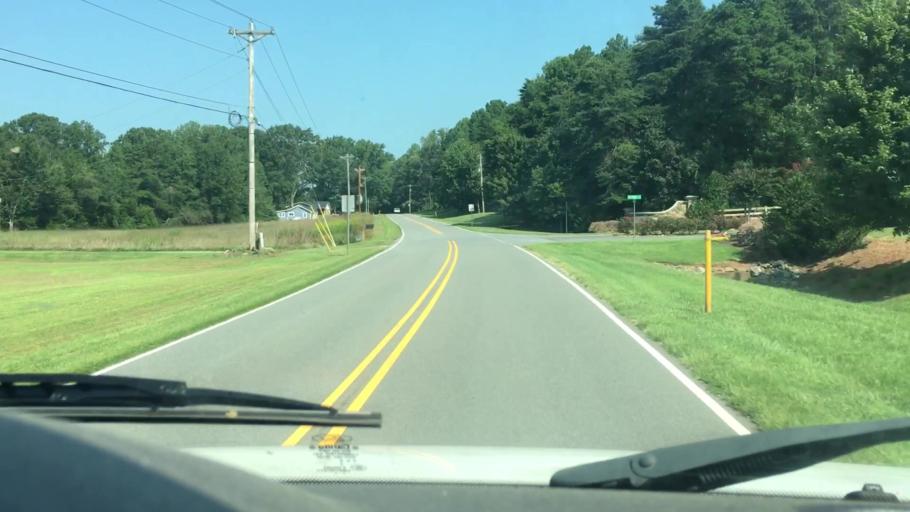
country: US
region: North Carolina
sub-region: Gaston County
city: Davidson
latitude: 35.4785
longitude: -80.7864
